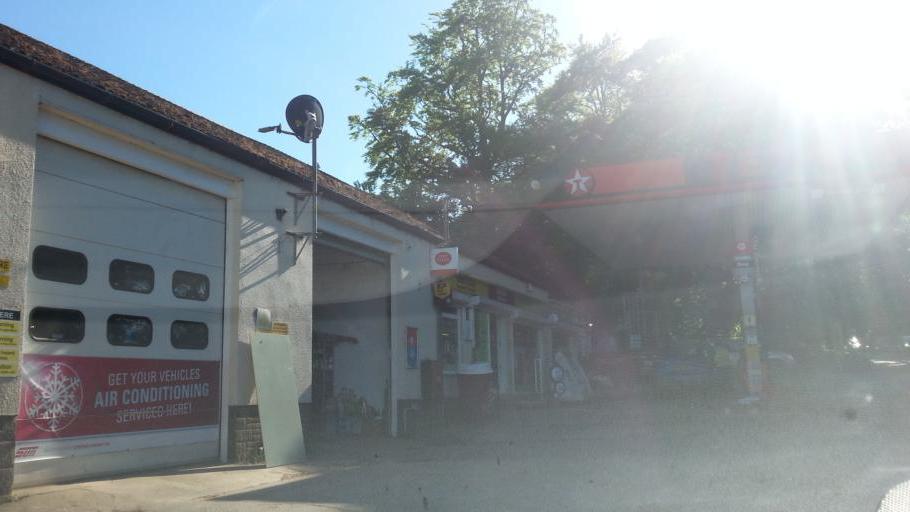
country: GB
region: England
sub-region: Somerset
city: Milborne Port
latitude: 50.9651
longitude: -2.4675
